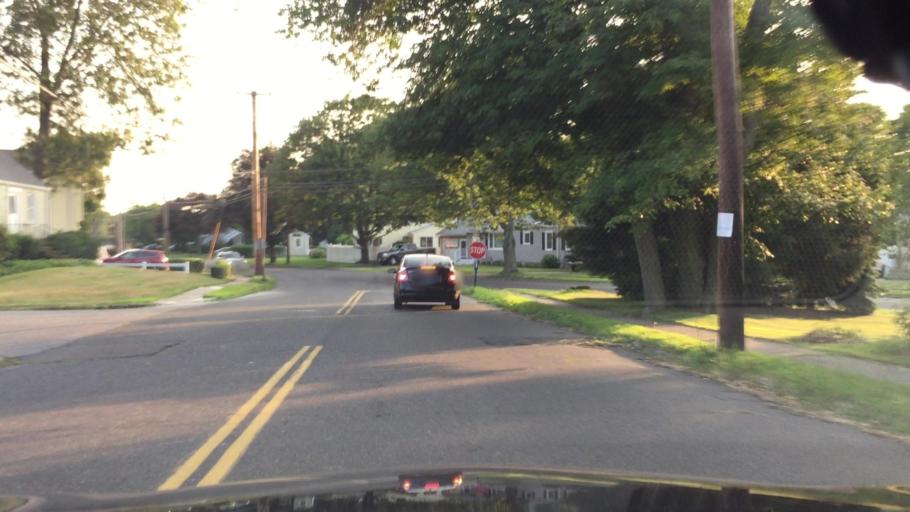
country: US
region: Connecticut
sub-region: New Haven County
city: City of Milford (balance)
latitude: 41.2060
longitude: -73.0822
